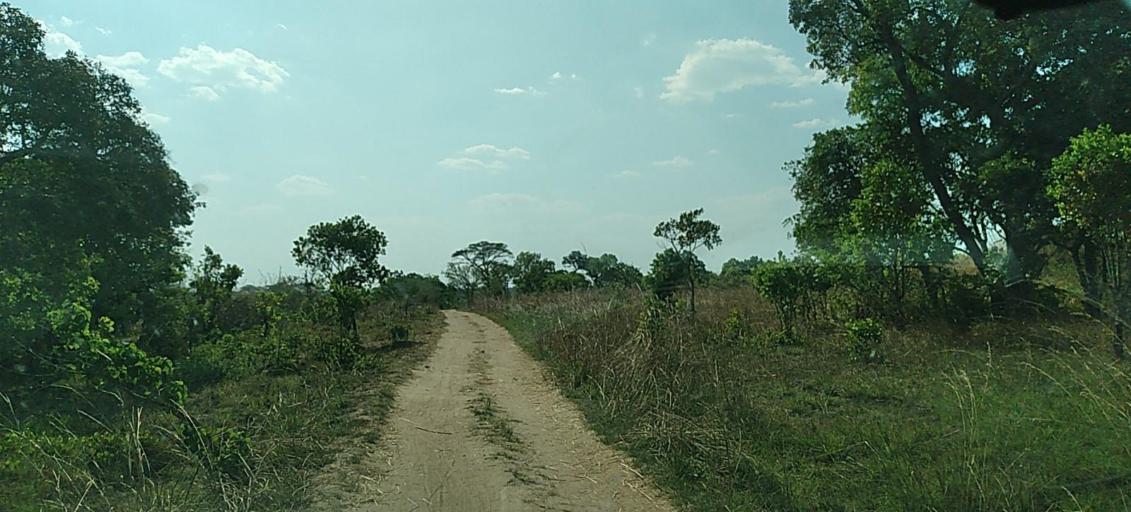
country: ZM
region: North-Western
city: Kalengwa
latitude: -13.1162
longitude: 24.9960
